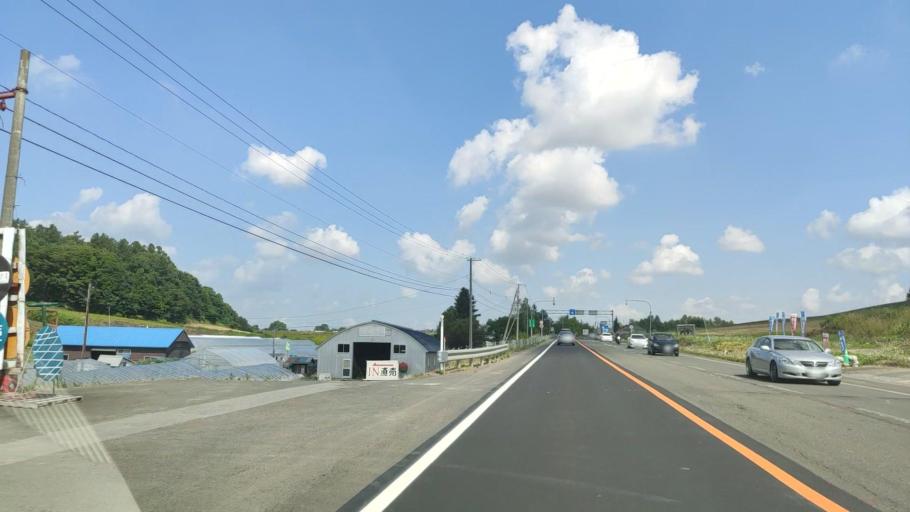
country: JP
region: Hokkaido
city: Shimo-furano
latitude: 43.5393
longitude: 142.4390
